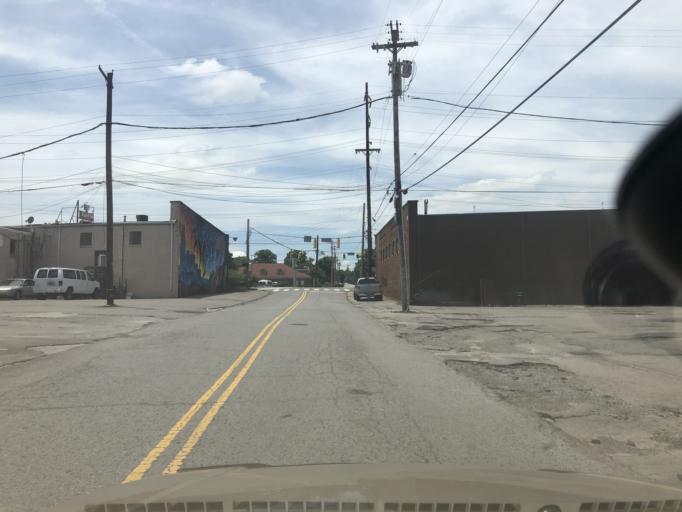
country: US
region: Tennessee
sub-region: Davidson County
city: Goodlettsville
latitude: 36.2584
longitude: -86.7126
